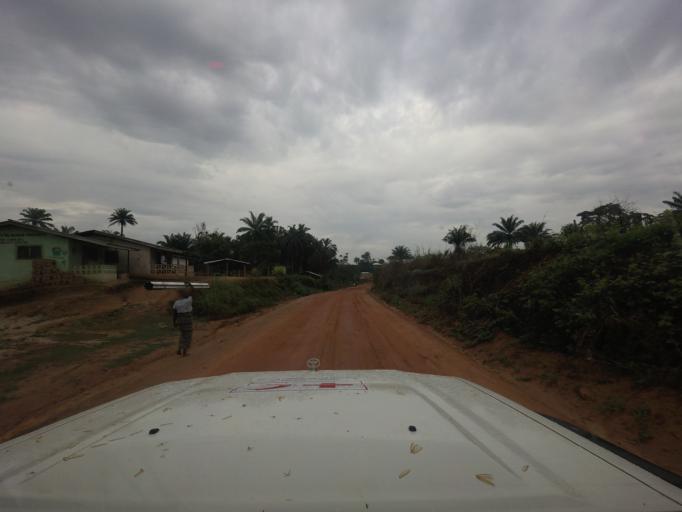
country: LR
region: Lofa
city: Voinjama
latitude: 8.4163
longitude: -9.7638
